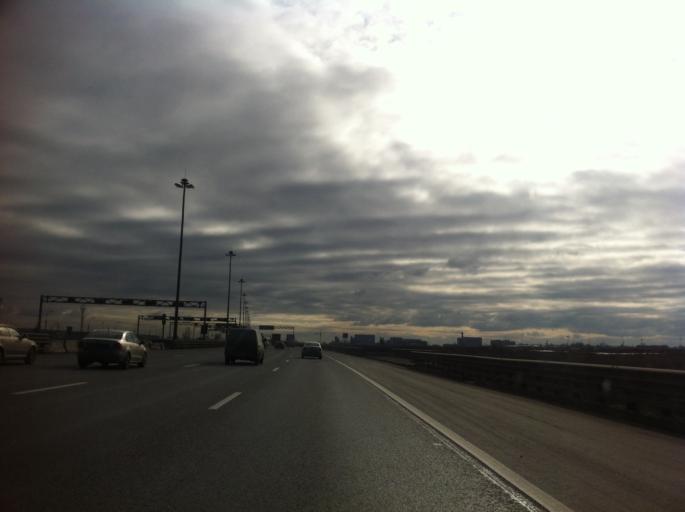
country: RU
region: St.-Petersburg
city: Dachnoye
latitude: 59.8261
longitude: 30.2916
